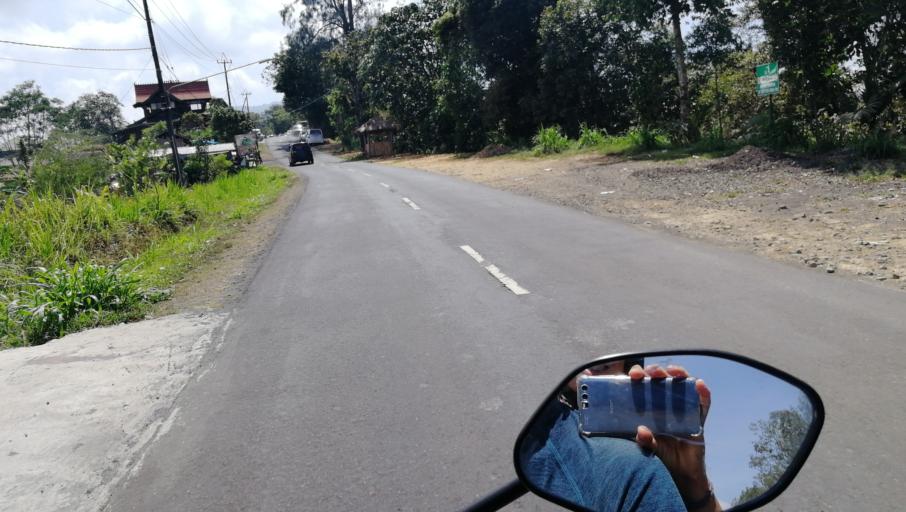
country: ID
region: Bali
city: Munduk
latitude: -8.2380
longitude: 115.1188
